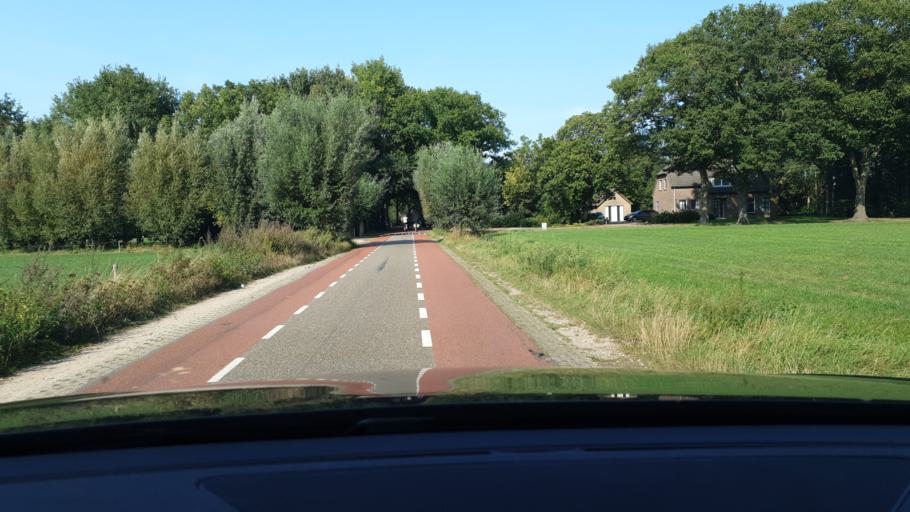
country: NL
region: North Brabant
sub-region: Gemeente Bernheze
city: Loosbroek
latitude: 51.7047
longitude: 5.5052
